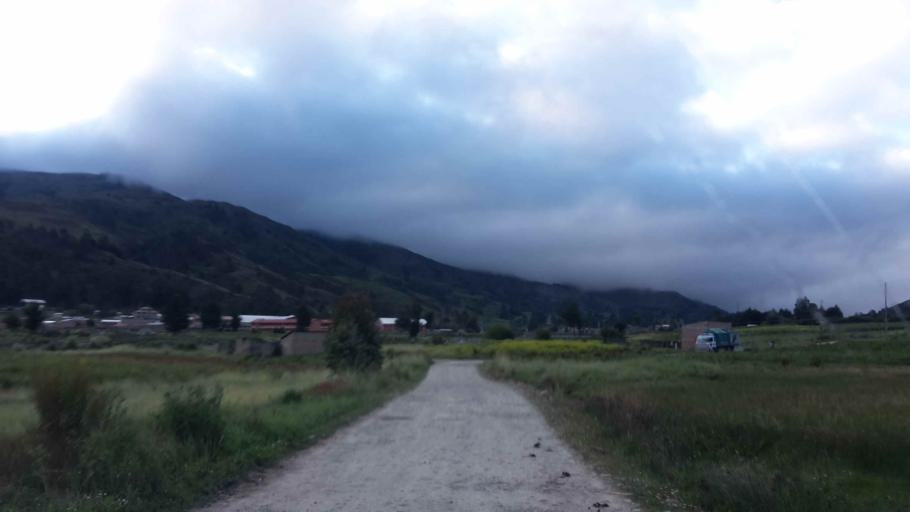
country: BO
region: Cochabamba
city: Colomi
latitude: -17.2757
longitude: -65.9190
